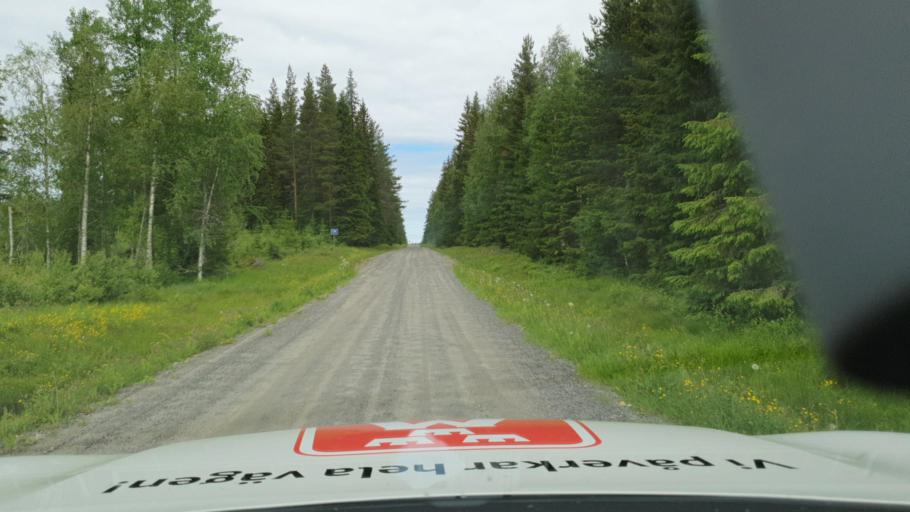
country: SE
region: Vaesterbotten
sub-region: Skelleftea Kommun
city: Langsele
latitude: 64.4616
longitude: 20.2790
